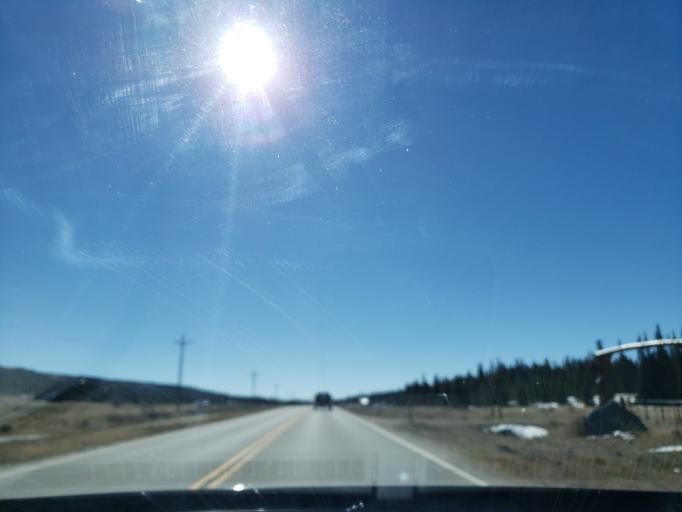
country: US
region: Colorado
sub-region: Park County
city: Fairplay
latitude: 39.2662
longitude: -106.0448
